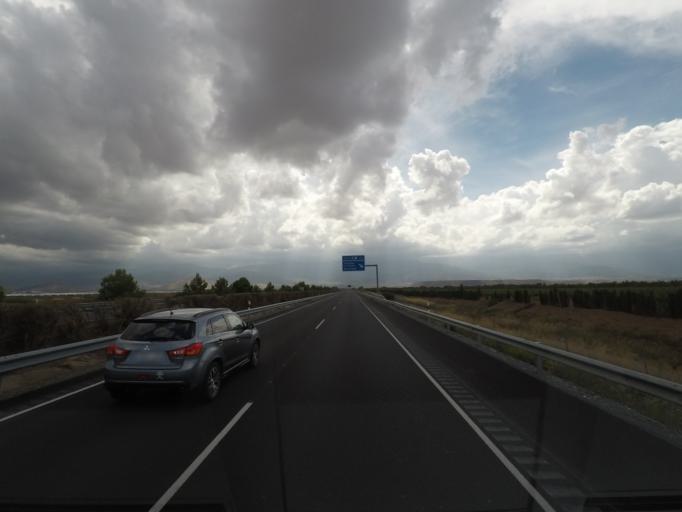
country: ES
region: Andalusia
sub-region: Provincia de Granada
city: Albunan
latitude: 37.2406
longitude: -3.0821
